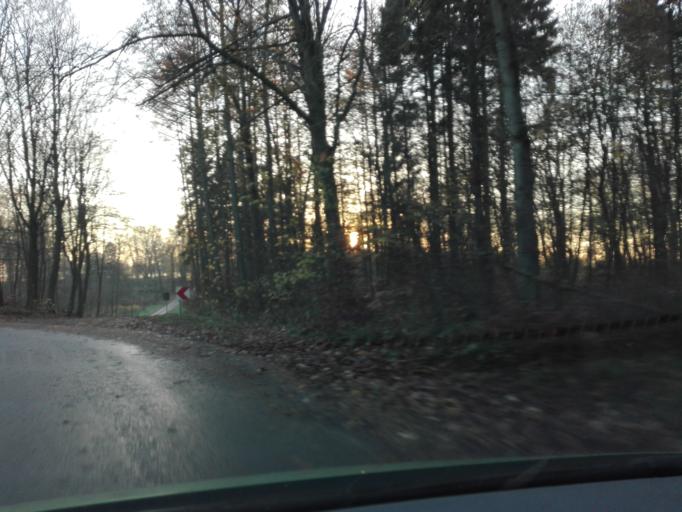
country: DK
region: Central Jutland
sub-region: Skanderborg Kommune
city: Galten
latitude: 56.1765
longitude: 9.9200
